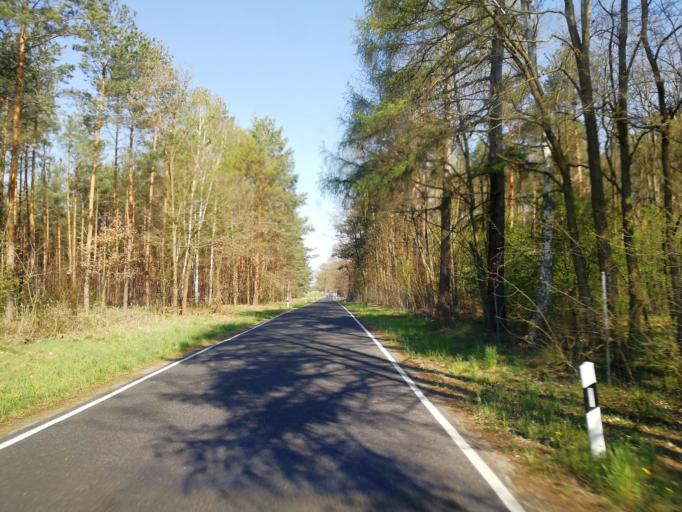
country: DE
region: Brandenburg
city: Bronkow
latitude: 51.7139
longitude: 13.8661
